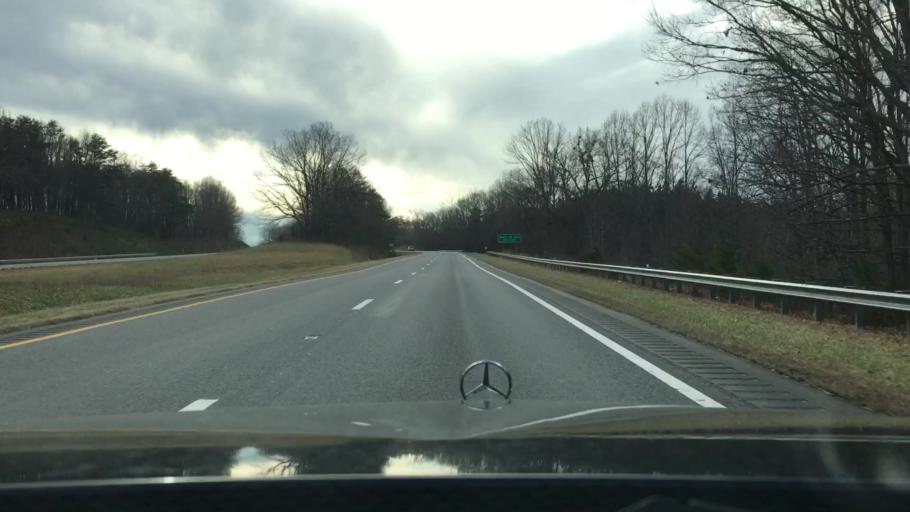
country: US
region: Virginia
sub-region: Pittsylvania County
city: Gretna
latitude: 36.9617
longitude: -79.3737
